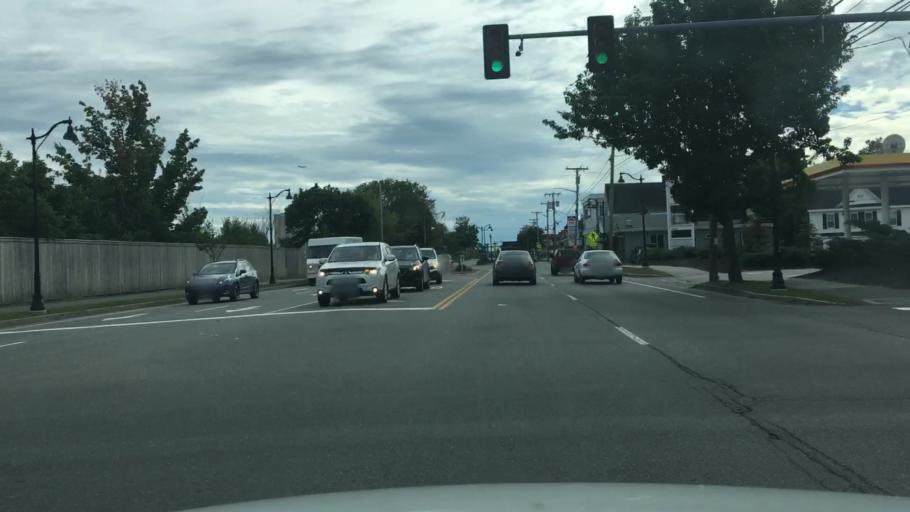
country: US
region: Maine
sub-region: Penobscot County
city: Bangor
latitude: 44.7932
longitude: -68.7756
